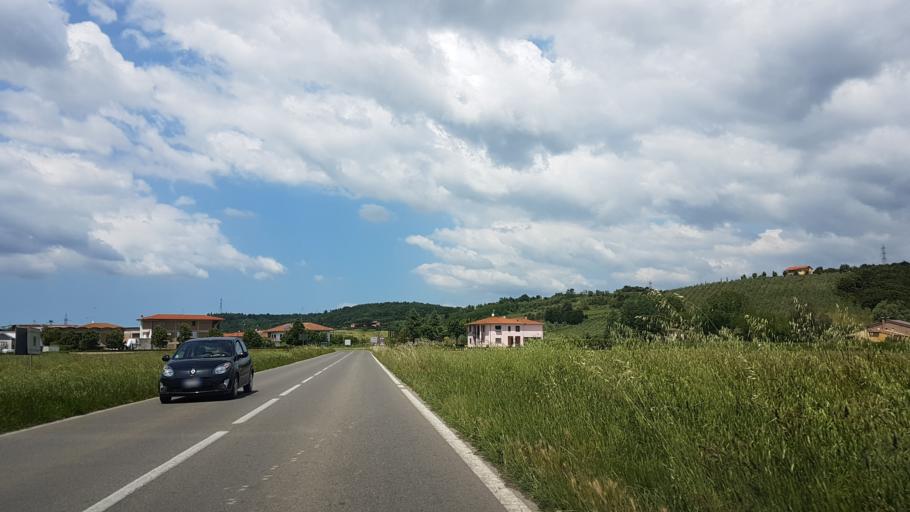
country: IT
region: Tuscany
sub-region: Province of Pisa
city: Fauglia
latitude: 43.5500
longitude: 10.5143
